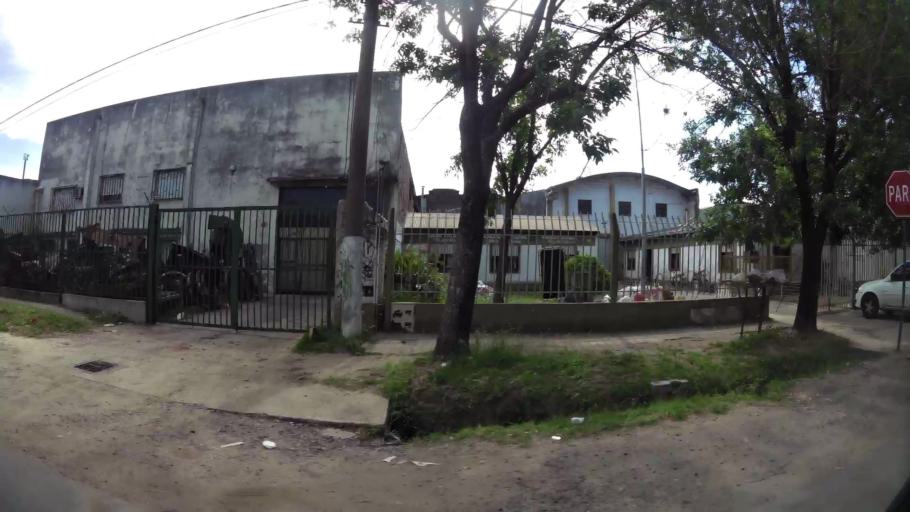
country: AR
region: Santa Fe
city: Granadero Baigorria
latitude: -32.9212
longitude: -60.7159
